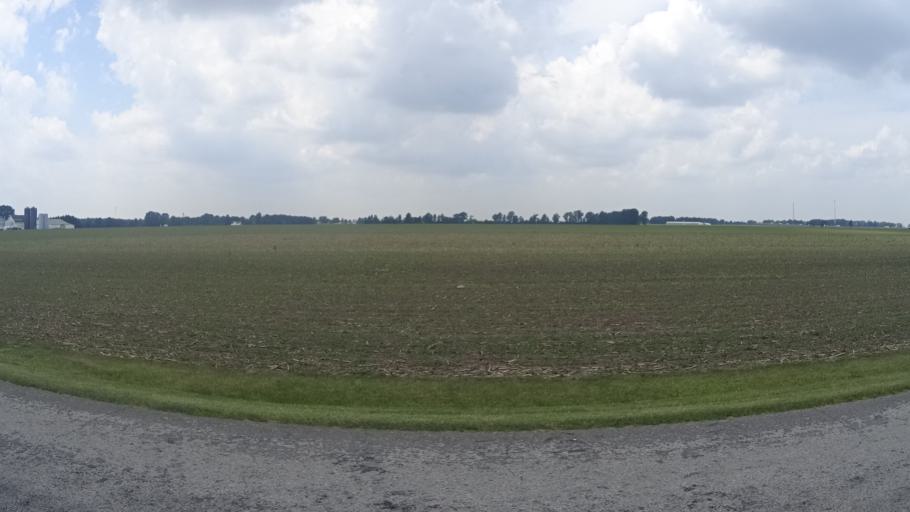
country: US
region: Ohio
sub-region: Erie County
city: Milan
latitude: 41.3271
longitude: -82.6736
